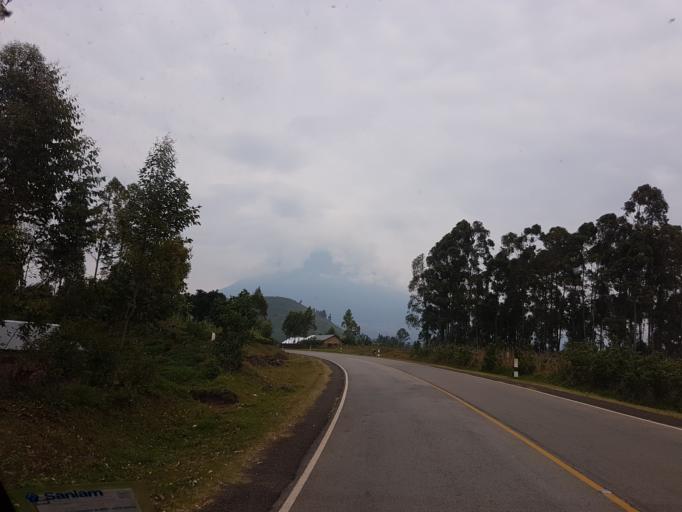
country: UG
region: Western Region
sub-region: Kisoro District
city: Kisoro
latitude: -1.3086
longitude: 29.7214
